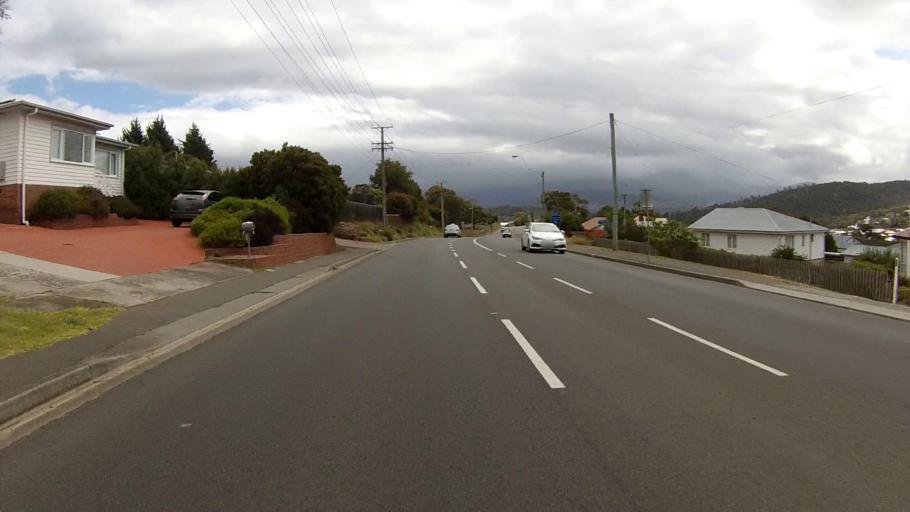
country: AU
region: Tasmania
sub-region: Clarence
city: Warrane
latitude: -42.8593
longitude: 147.3838
